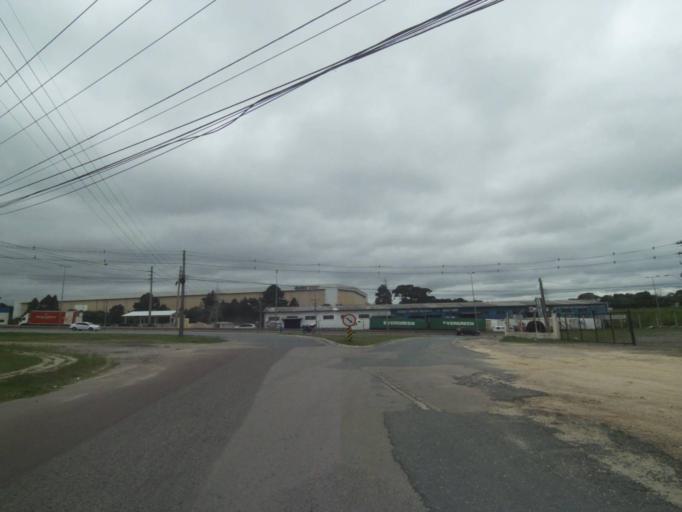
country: BR
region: Parana
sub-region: Sao Jose Dos Pinhais
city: Sao Jose dos Pinhais
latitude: -25.5608
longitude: -49.3085
